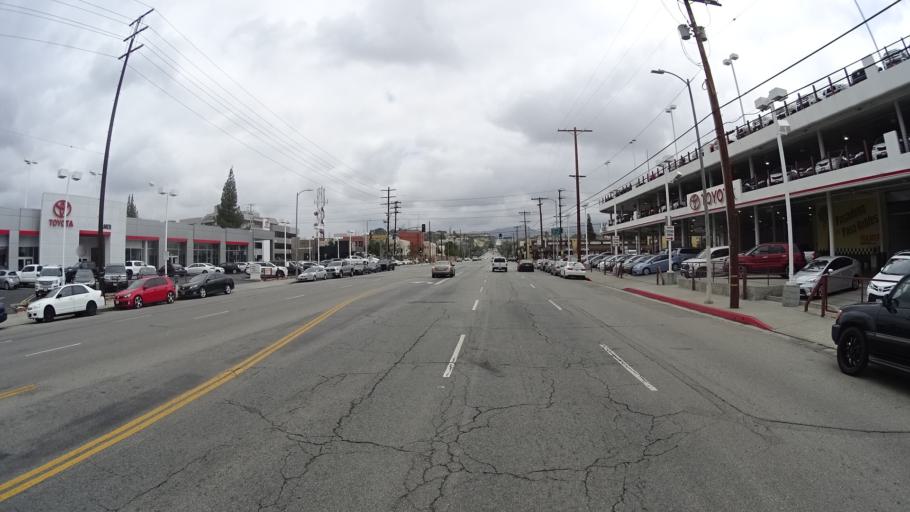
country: US
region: California
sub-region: Los Angeles County
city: San Fernando
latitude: 34.2713
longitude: -118.4673
